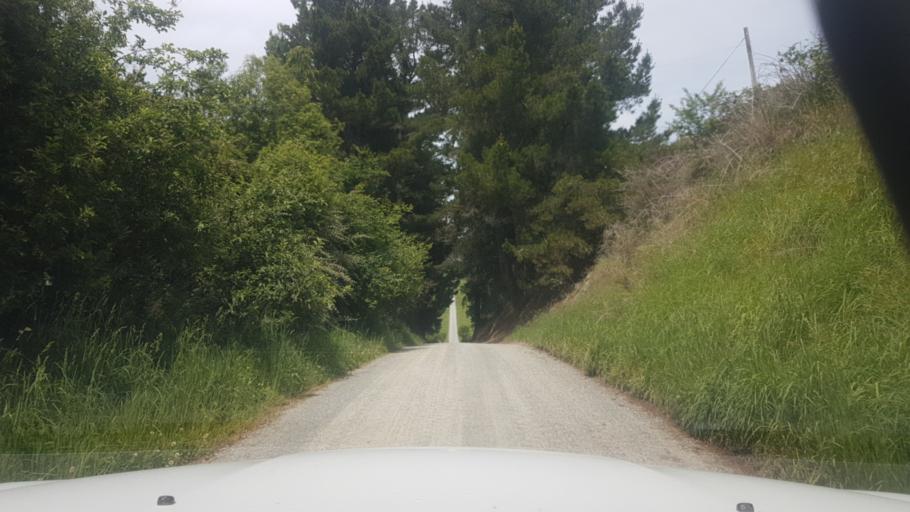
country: NZ
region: Canterbury
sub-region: Timaru District
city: Pleasant Point
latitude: -44.1953
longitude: 171.0914
